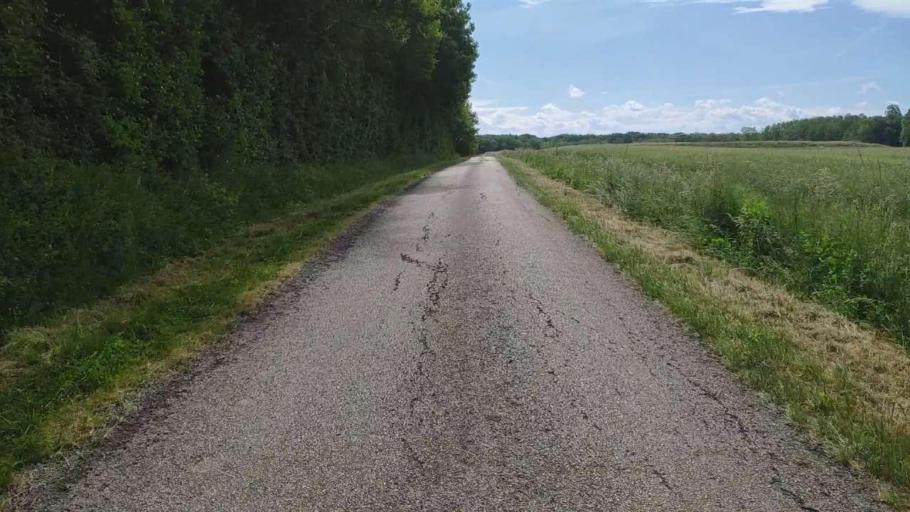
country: FR
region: Franche-Comte
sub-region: Departement du Jura
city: Bletterans
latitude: 46.6884
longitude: 5.4265
